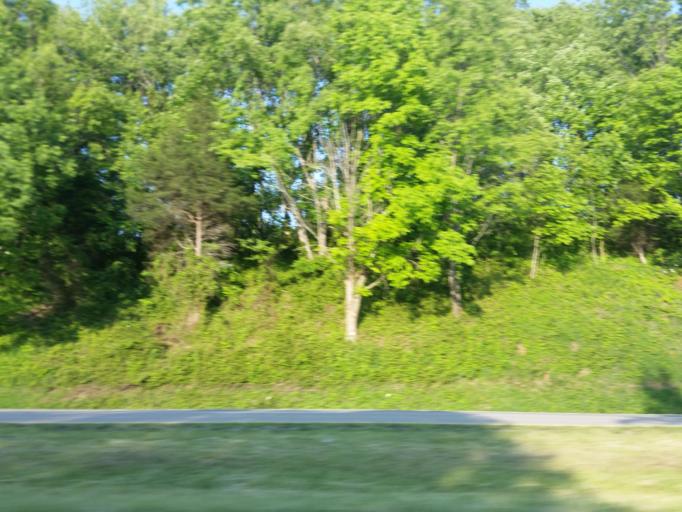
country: US
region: Virginia
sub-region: Russell County
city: Lebanon
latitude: 36.8658
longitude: -82.1124
